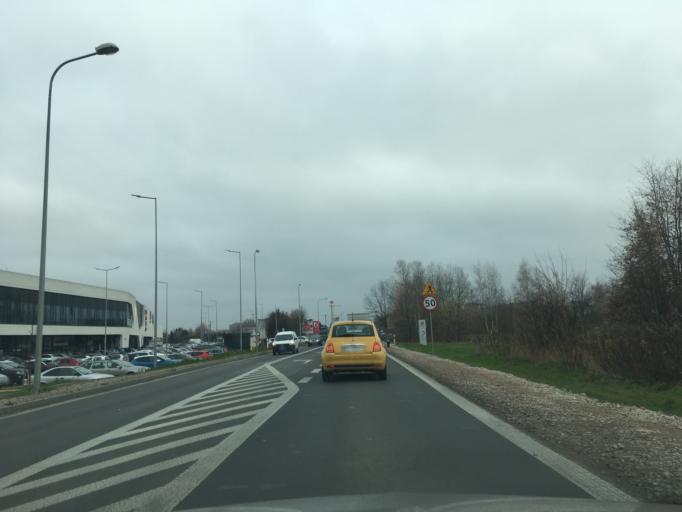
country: PL
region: Masovian Voivodeship
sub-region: Powiat piaseczynski
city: Piaseczno
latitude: 52.0822
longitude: 21.0096
